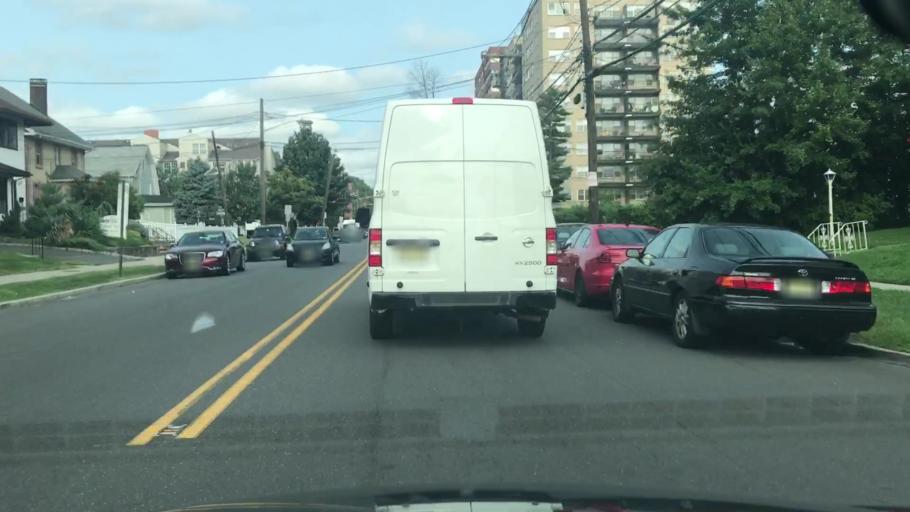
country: US
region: New Jersey
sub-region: Union County
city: Elizabeth
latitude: 40.6816
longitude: -74.2097
